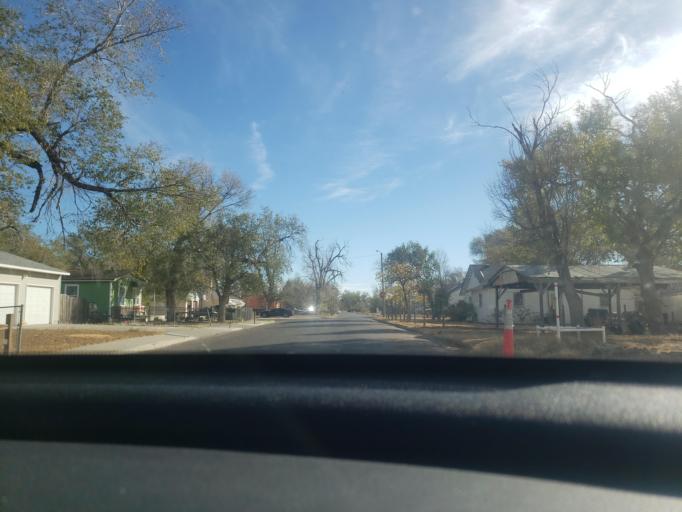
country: US
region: Kansas
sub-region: Finney County
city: Garden City
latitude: 37.9770
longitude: -100.8800
